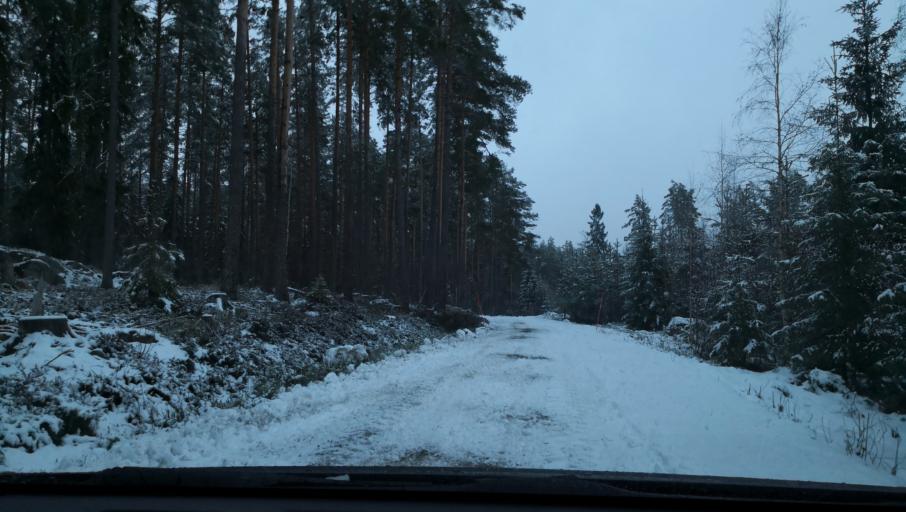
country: SE
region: Vaestmanland
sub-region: Kopings Kommun
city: Kolsva
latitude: 59.5665
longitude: 15.8221
